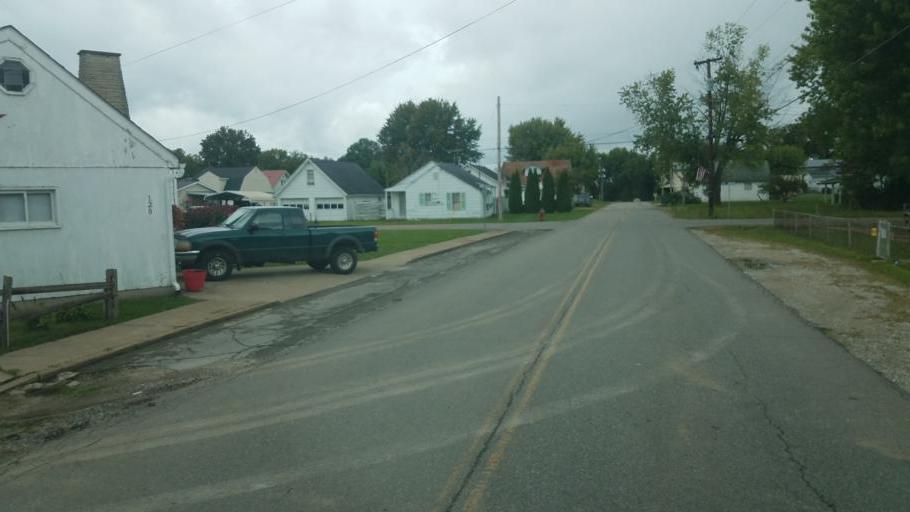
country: US
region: Kentucky
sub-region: Greenup County
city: South Shore
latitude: 38.7229
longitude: -82.9665
